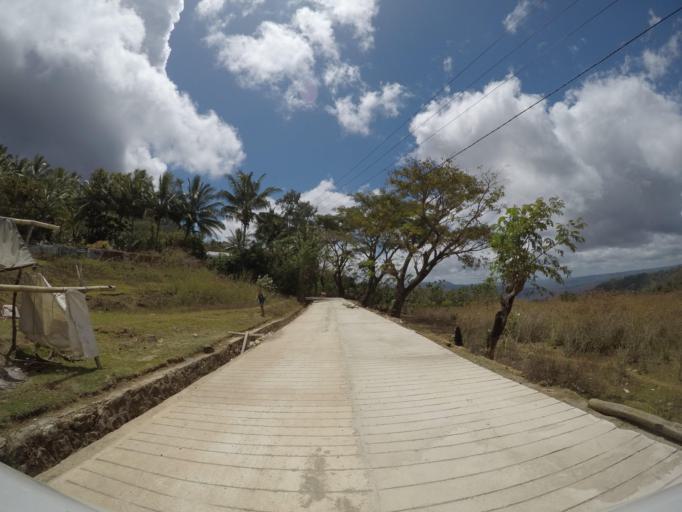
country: TL
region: Lautem
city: Lospalos
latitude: -8.5538
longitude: 126.8290
